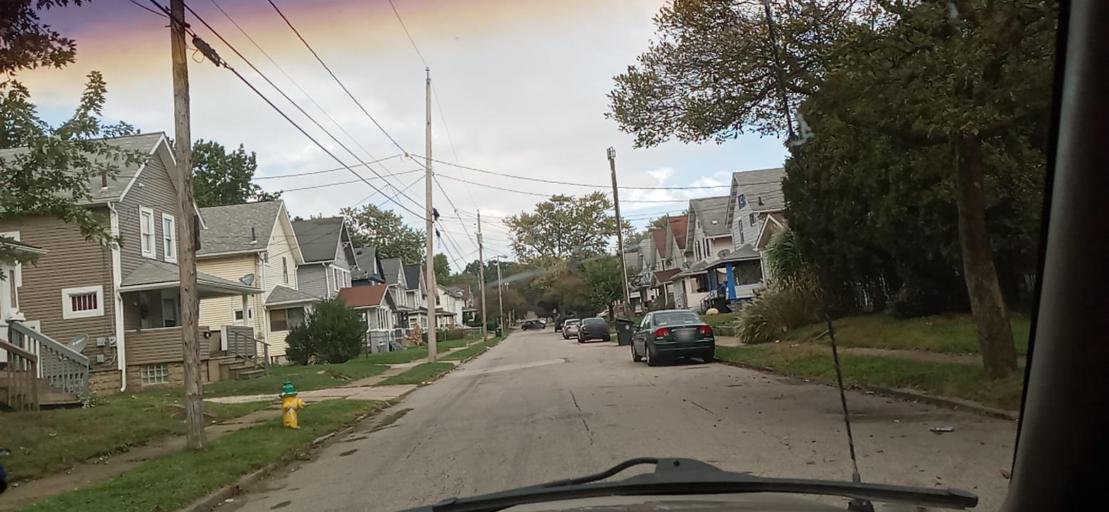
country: US
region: Ohio
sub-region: Summit County
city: Portage Lakes
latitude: 41.0406
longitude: -81.5523
